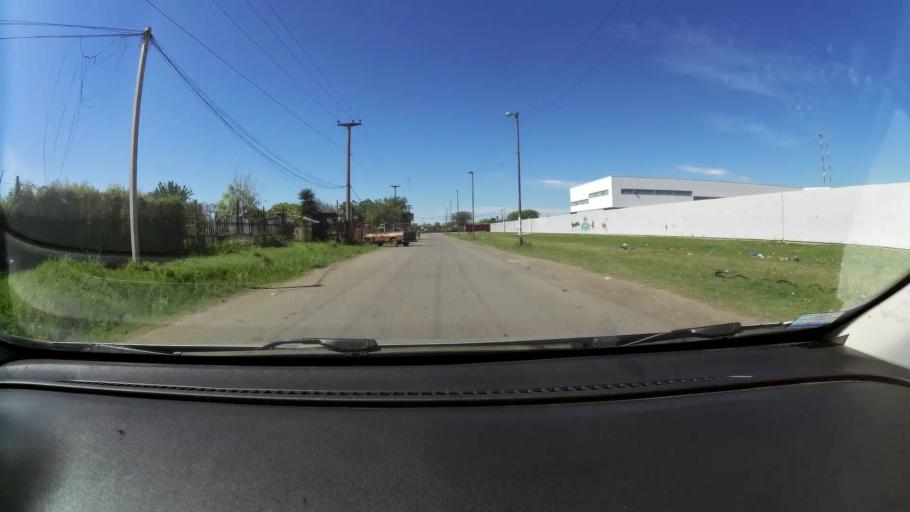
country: AR
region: Santa Fe
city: Perez
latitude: -32.9755
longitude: -60.7111
